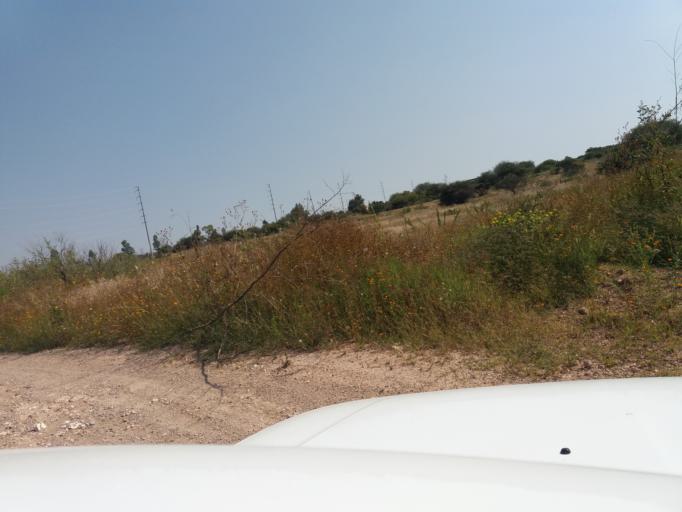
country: MX
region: Aguascalientes
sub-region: Aguascalientes
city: Penuelas (El Cienegal)
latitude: 21.7479
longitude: -102.2522
